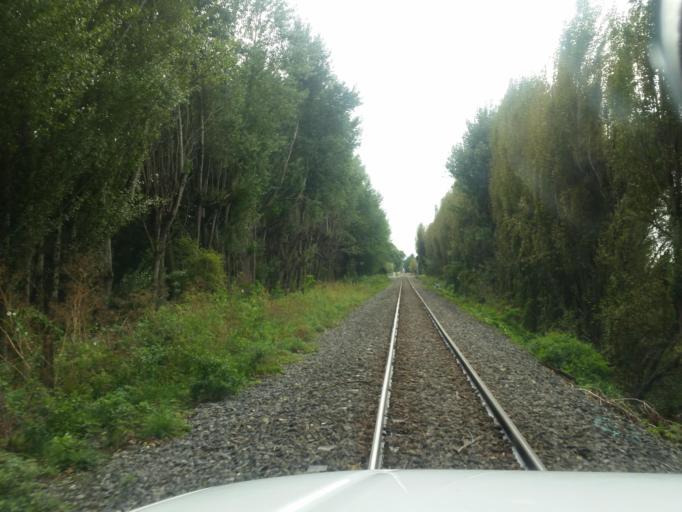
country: NZ
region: Canterbury
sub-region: Christchurch City
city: Christchurch
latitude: -43.4633
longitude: 172.6241
